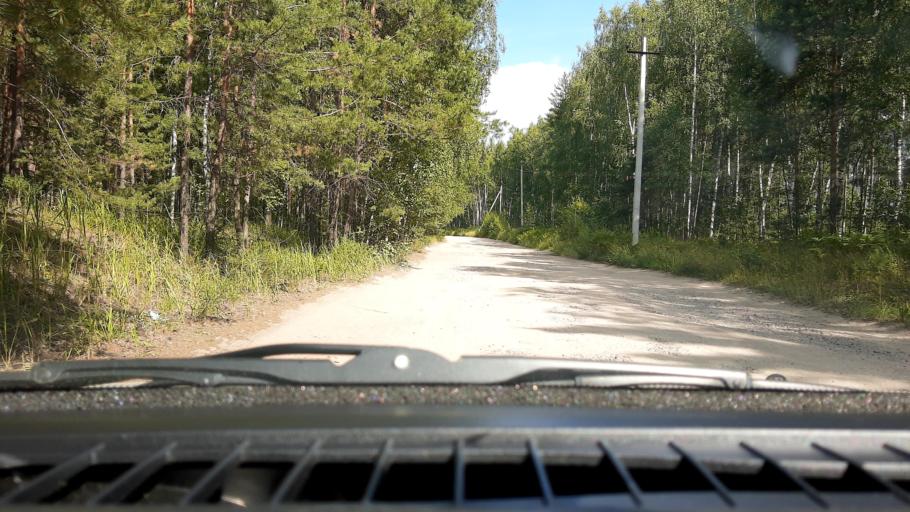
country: RU
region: Nizjnij Novgorod
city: Lukino
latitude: 56.3339
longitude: 43.6548
